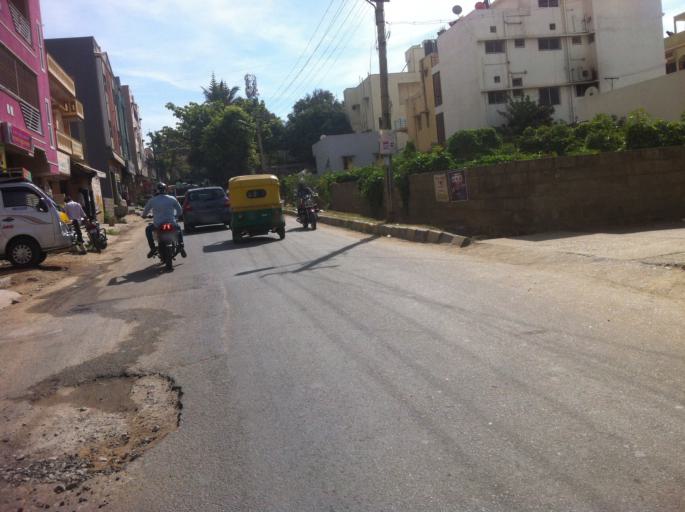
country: IN
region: Karnataka
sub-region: Bangalore Urban
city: Bangalore
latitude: 12.8923
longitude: 77.6157
